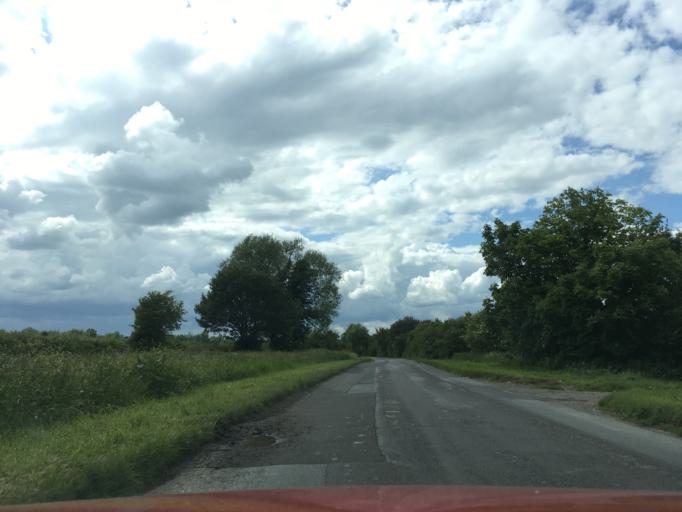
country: GB
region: England
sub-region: Wiltshire
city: Cricklade
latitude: 51.6280
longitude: -1.8655
